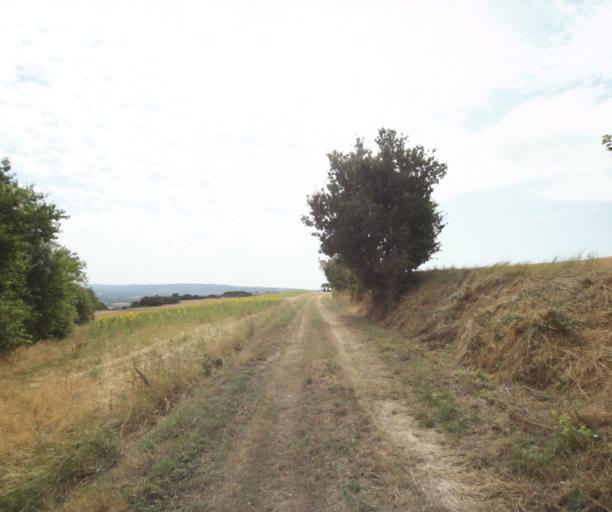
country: FR
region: Midi-Pyrenees
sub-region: Departement de la Haute-Garonne
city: Saint-Felix-Lauragais
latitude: 43.4493
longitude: 1.8942
